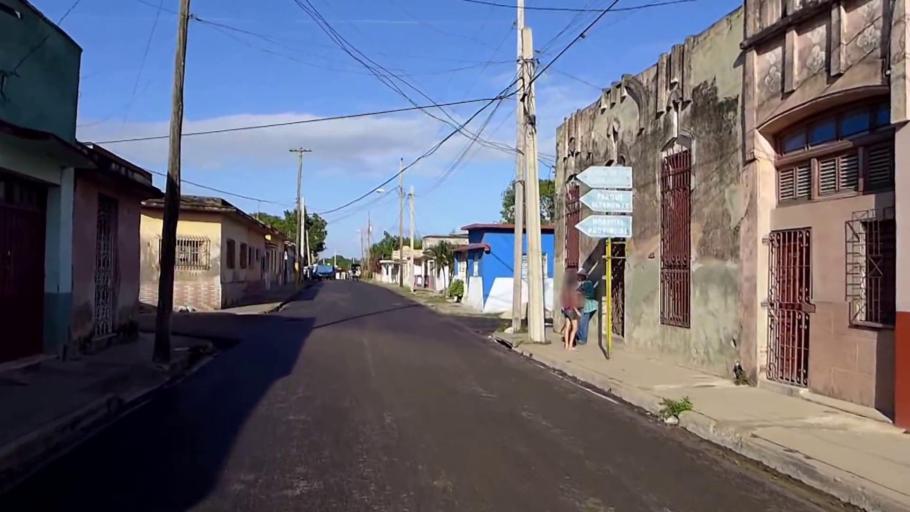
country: CU
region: Camaguey
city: Camaguey
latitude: 21.3859
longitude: -77.9254
